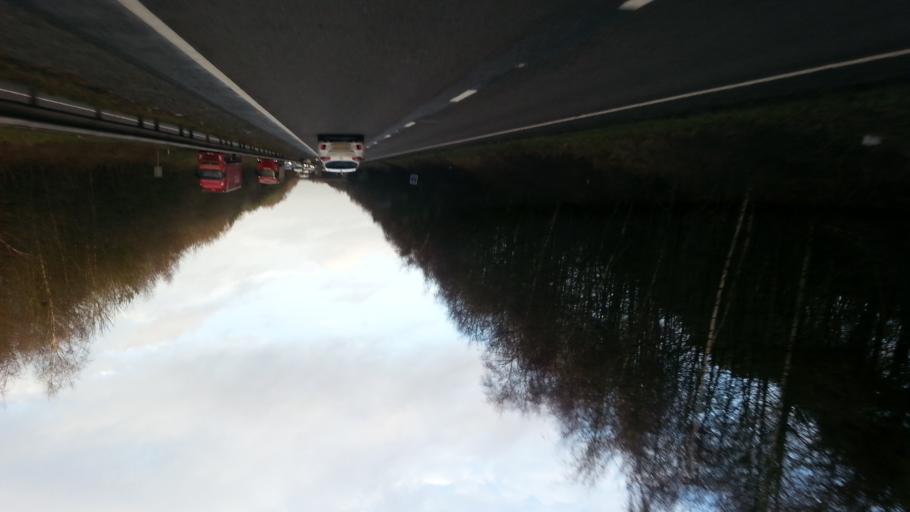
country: GB
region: England
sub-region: Derbyshire
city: Melbourne
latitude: 52.7786
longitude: -1.4184
